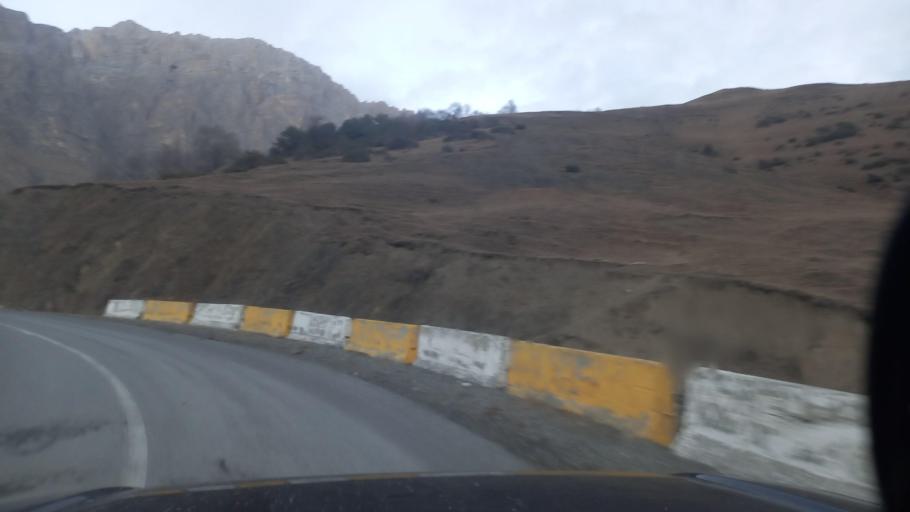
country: RU
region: Ingushetiya
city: Dzhayrakh
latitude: 42.8187
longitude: 44.8162
